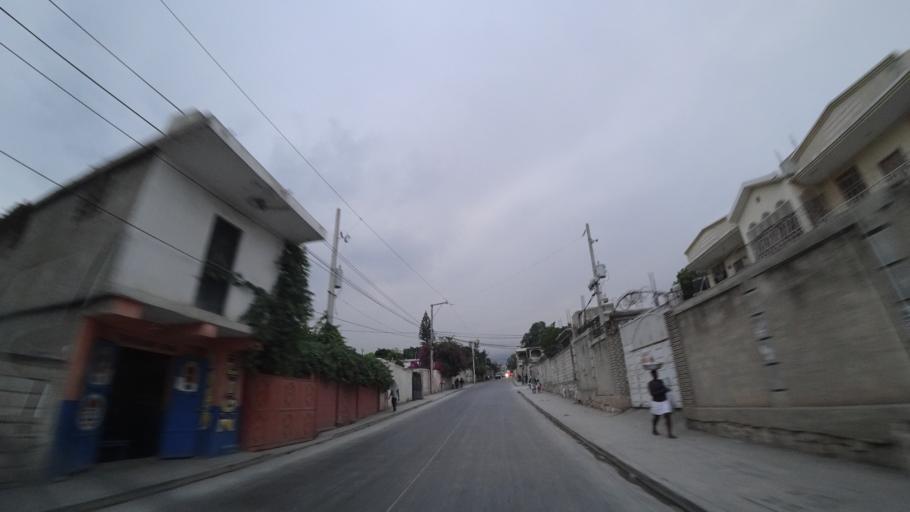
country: HT
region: Ouest
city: Delmas 73
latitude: 18.5446
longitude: -72.2867
